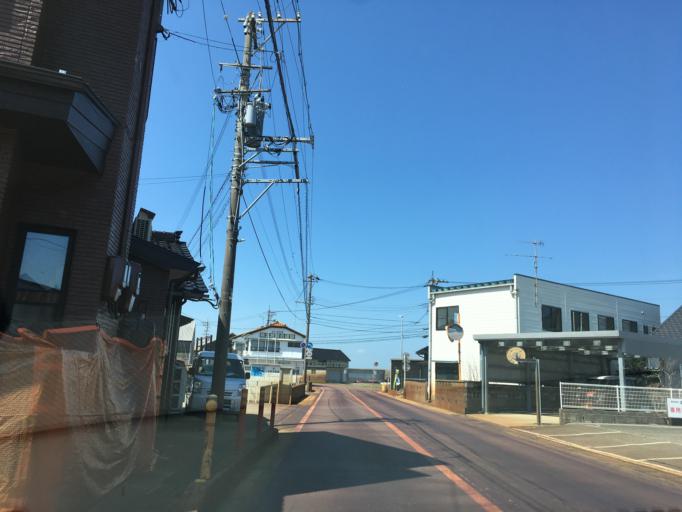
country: JP
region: Toyama
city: Kuragaki-kosugi
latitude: 36.7565
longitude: 137.1908
